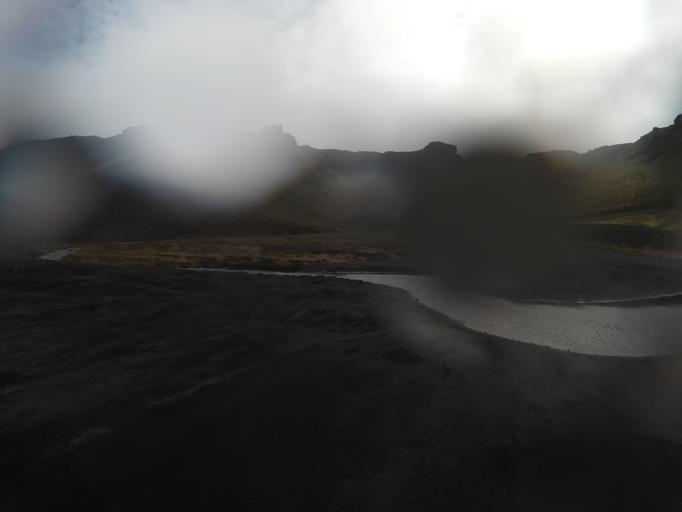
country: IS
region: South
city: Vestmannaeyjar
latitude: 63.9807
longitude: -18.8682
